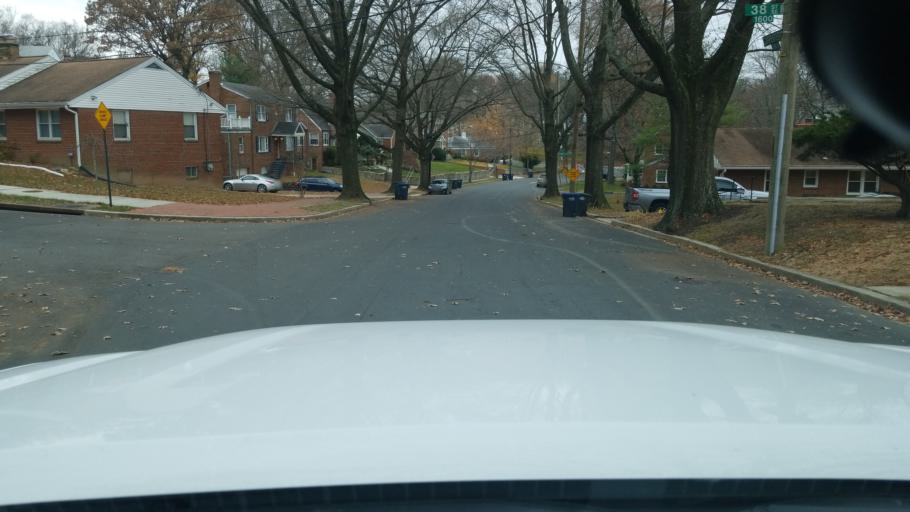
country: US
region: Maryland
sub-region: Prince George's County
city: Silver Hill
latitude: 38.8703
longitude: -76.9504
